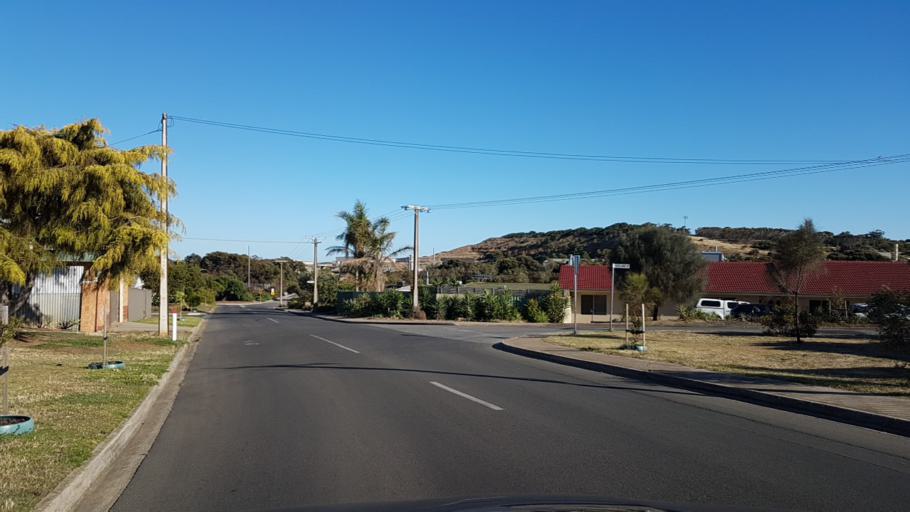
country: AU
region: South Australia
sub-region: Adelaide
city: Port Noarlunga
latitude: -35.1296
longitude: 138.4731
